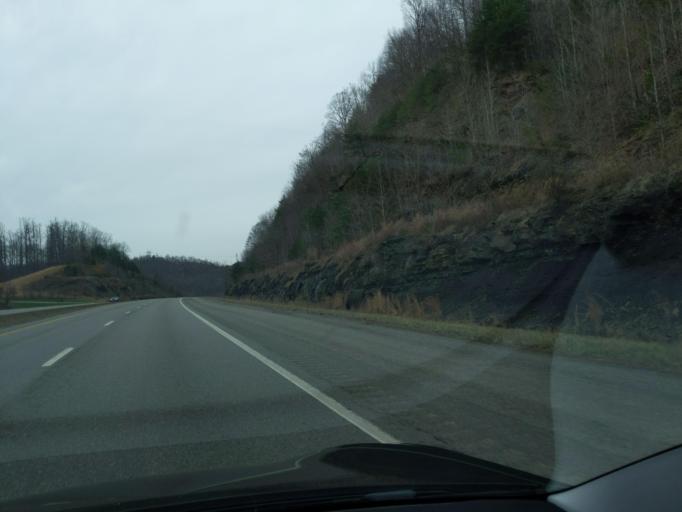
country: US
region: Kentucky
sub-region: Bell County
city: Pineville
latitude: 36.8069
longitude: -83.7593
